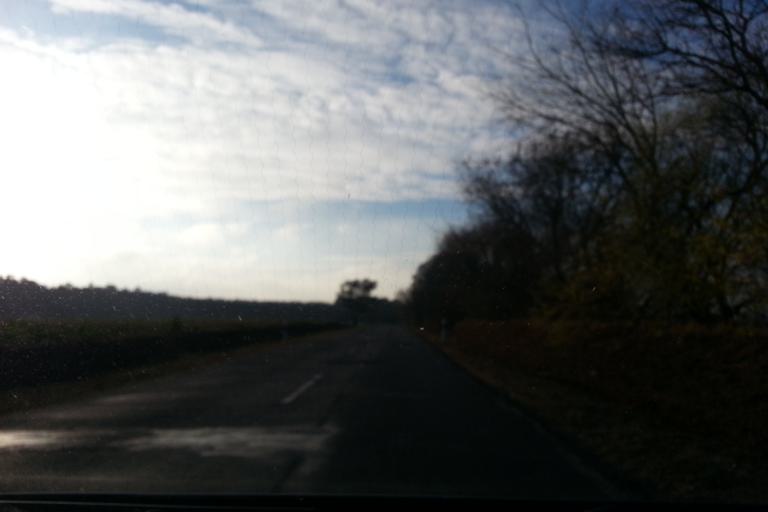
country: DE
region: Mecklenburg-Vorpommern
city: Ferdinandshof
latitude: 53.6326
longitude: 13.8175
